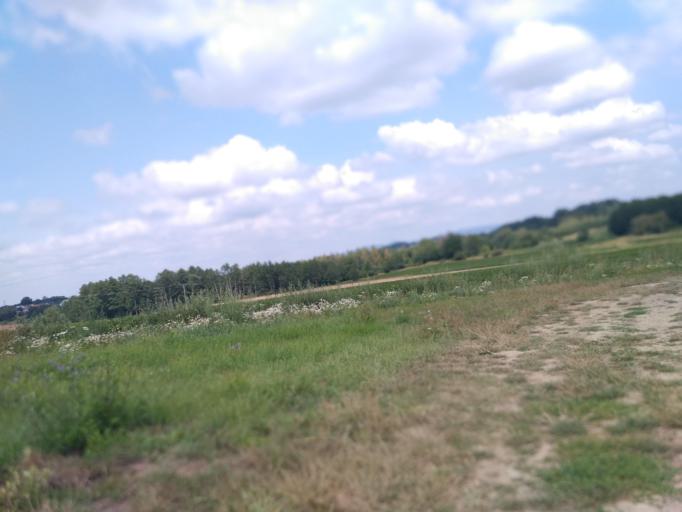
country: PL
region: Subcarpathian Voivodeship
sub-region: Powiat krosnienski
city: Iwonicz-Zdroj
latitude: 49.5906
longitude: 21.8080
